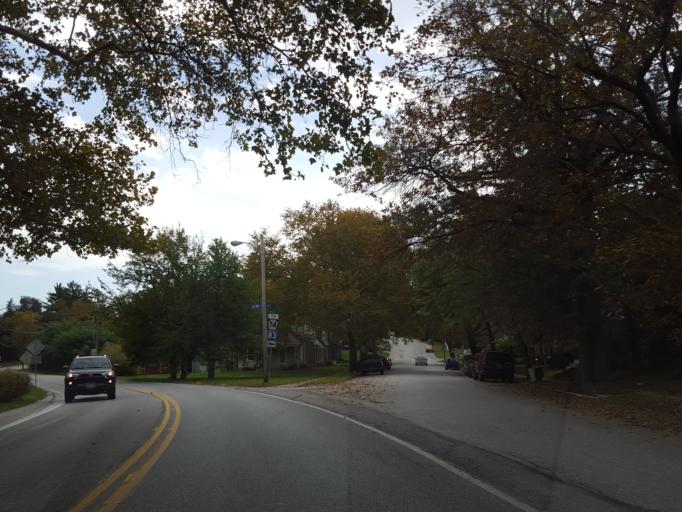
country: US
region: Pennsylvania
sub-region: York County
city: Valley View
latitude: 39.9565
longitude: -76.6986
